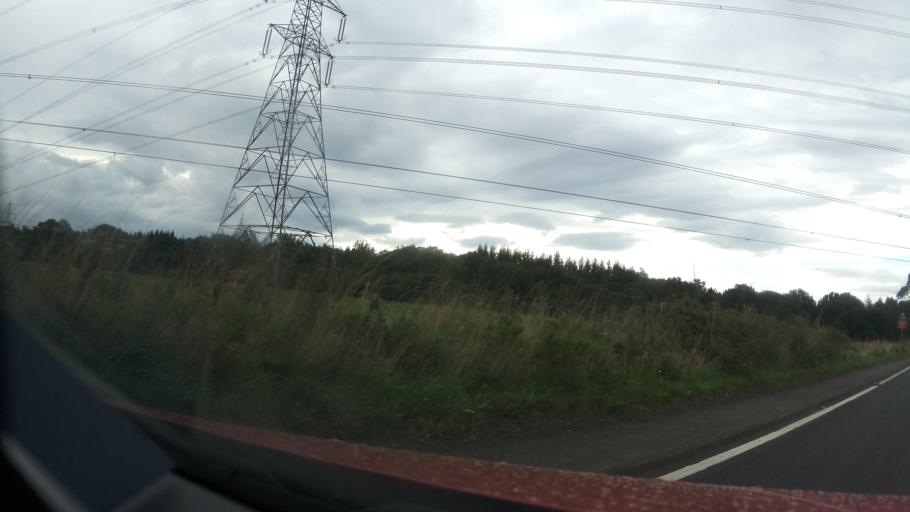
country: GB
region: Scotland
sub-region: Fife
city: Kincardine
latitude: 56.0889
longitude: -3.7191
